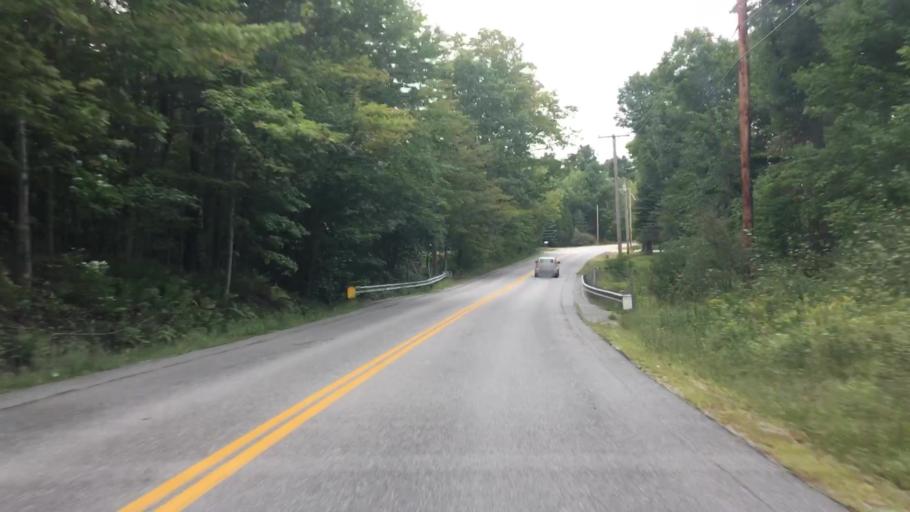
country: US
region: Maine
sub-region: Cumberland County
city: Yarmouth
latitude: 43.8454
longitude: -70.2133
